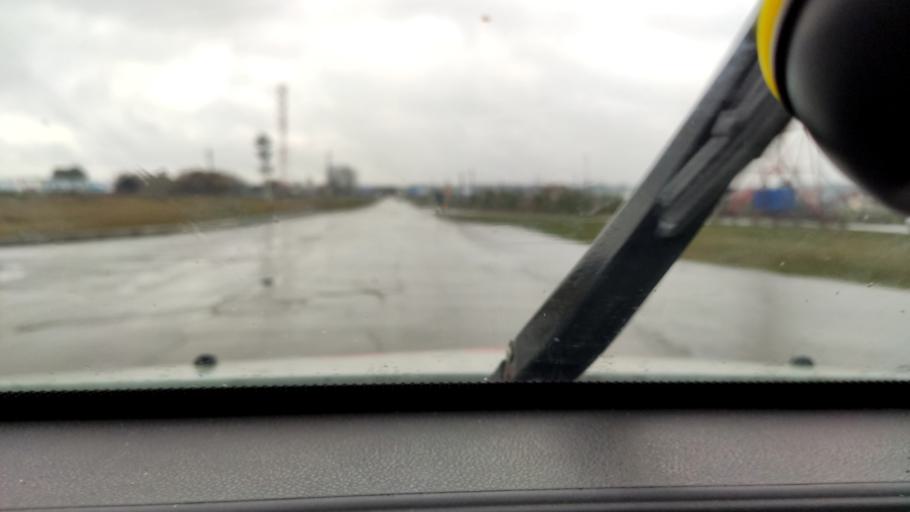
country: RU
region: Samara
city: Povolzhskiy
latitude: 53.6473
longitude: 49.6791
